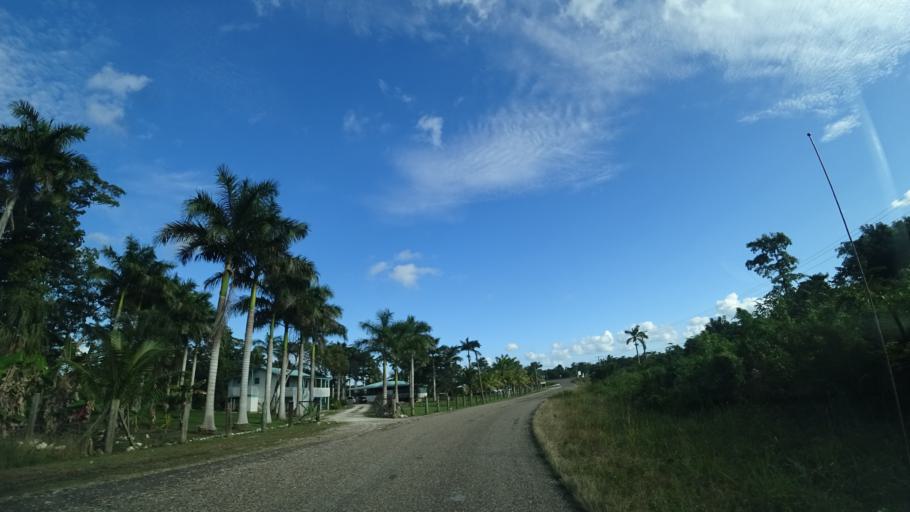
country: BZ
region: Belize
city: Belize City
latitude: 17.5712
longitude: -88.3886
